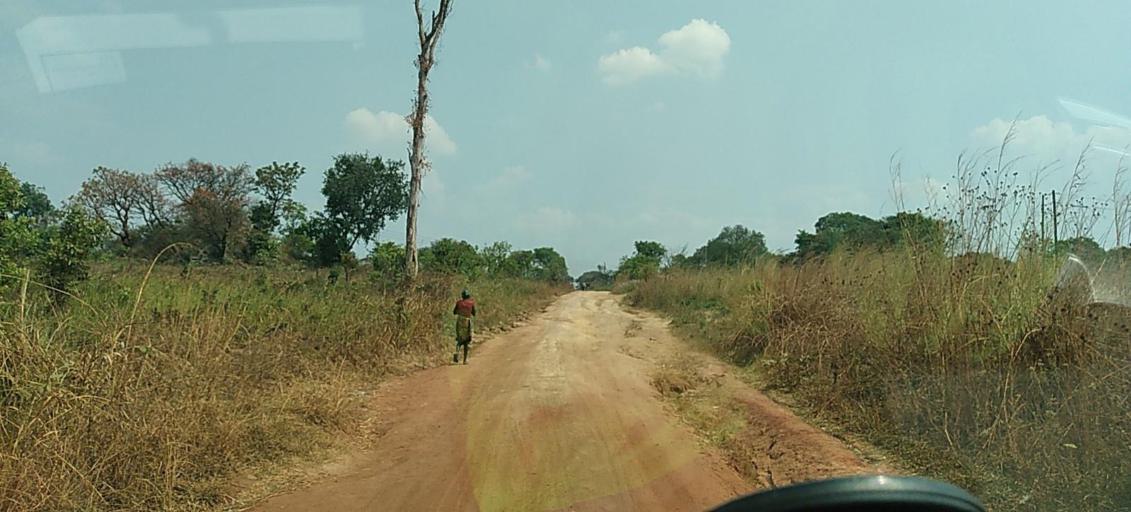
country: ZM
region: North-Western
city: Solwezi
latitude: -12.1135
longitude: 26.3673
